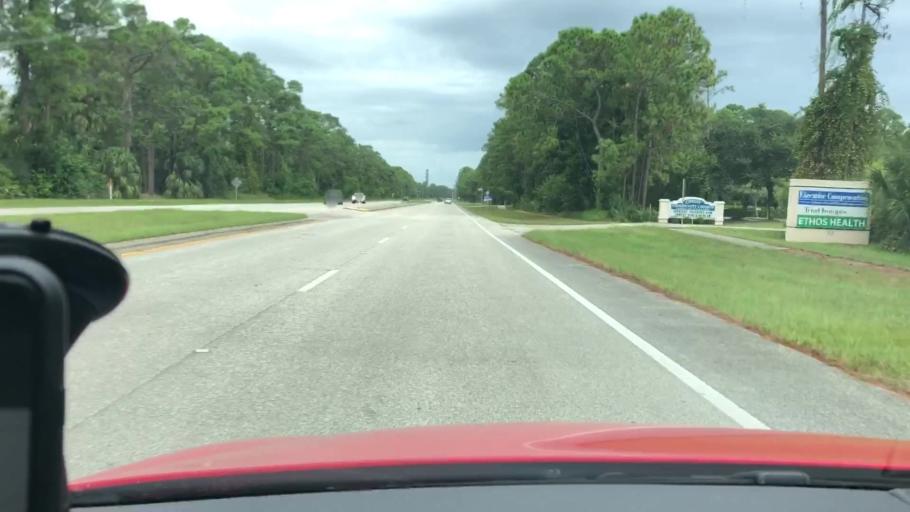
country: US
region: Florida
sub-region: Volusia County
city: Daytona Beach
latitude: 29.1906
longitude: -81.0824
